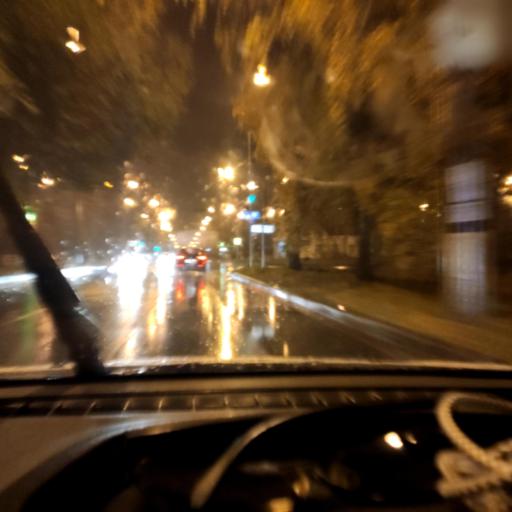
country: RU
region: Samara
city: Tol'yatti
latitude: 53.5061
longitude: 49.3908
